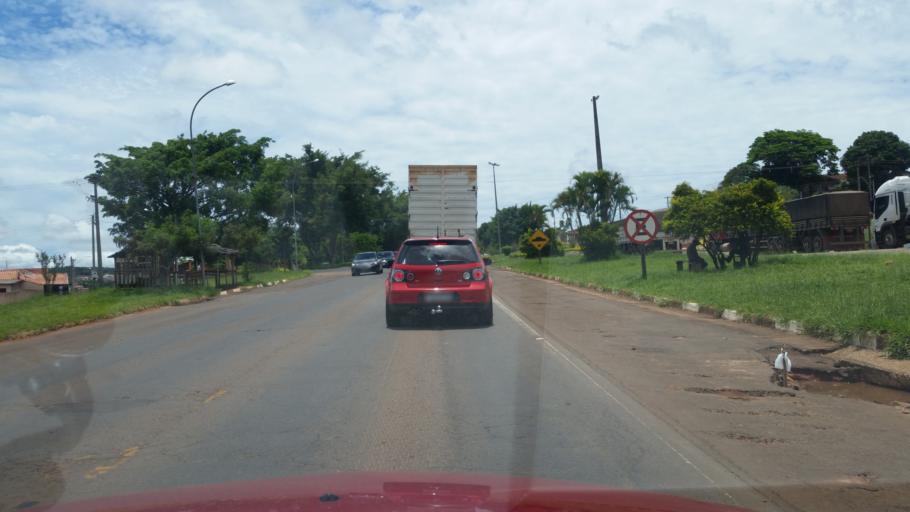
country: BR
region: Sao Paulo
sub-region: Itai
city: Itai
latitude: -23.4140
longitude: -49.0930
